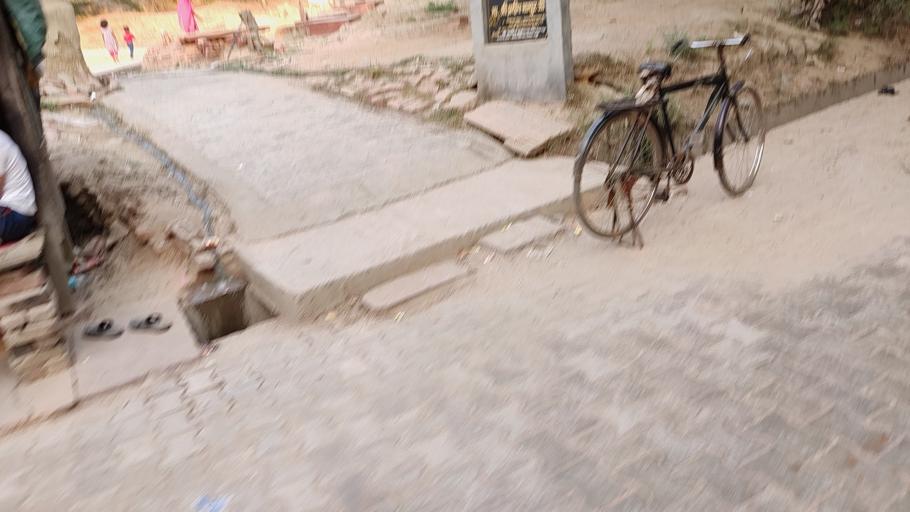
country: IN
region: Uttar Pradesh
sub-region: Mathura
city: Mathura
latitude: 27.5138
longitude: 77.6749
